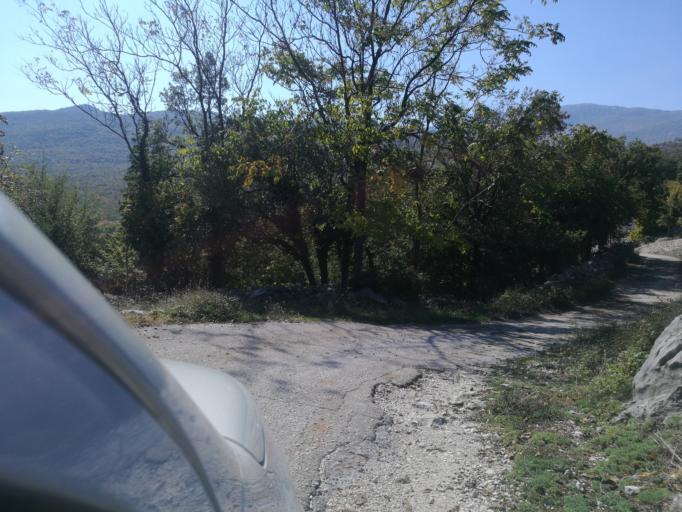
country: HR
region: Splitsko-Dalmatinska
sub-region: Grad Omis
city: Omis
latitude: 43.5176
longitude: 16.7271
